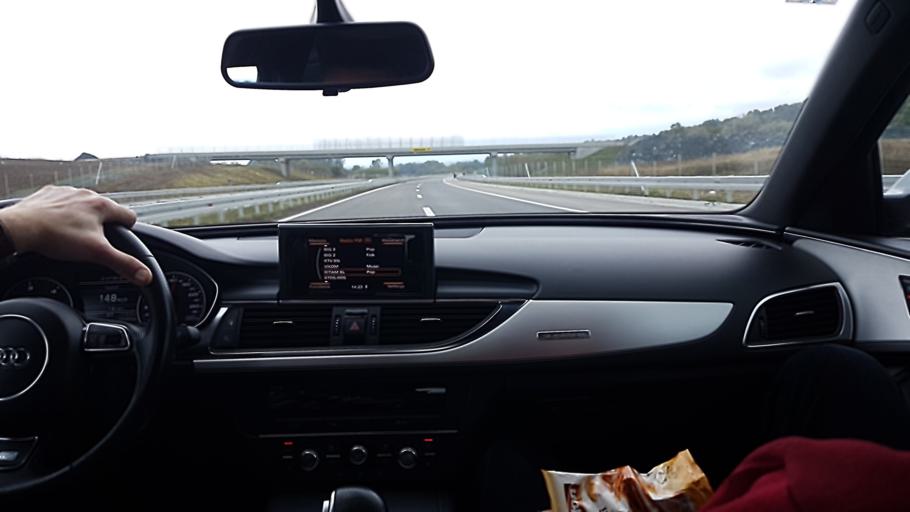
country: BA
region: Republika Srpska
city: Prnjavor
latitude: 44.8485
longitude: 17.7460
